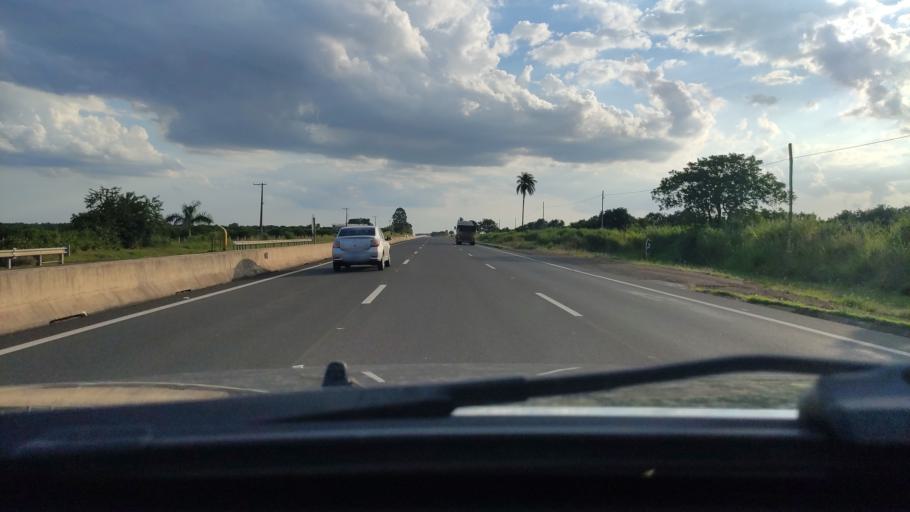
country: BR
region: Sao Paulo
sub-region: Mogi-Mirim
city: Mogi Mirim
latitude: -22.4534
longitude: -47.0890
